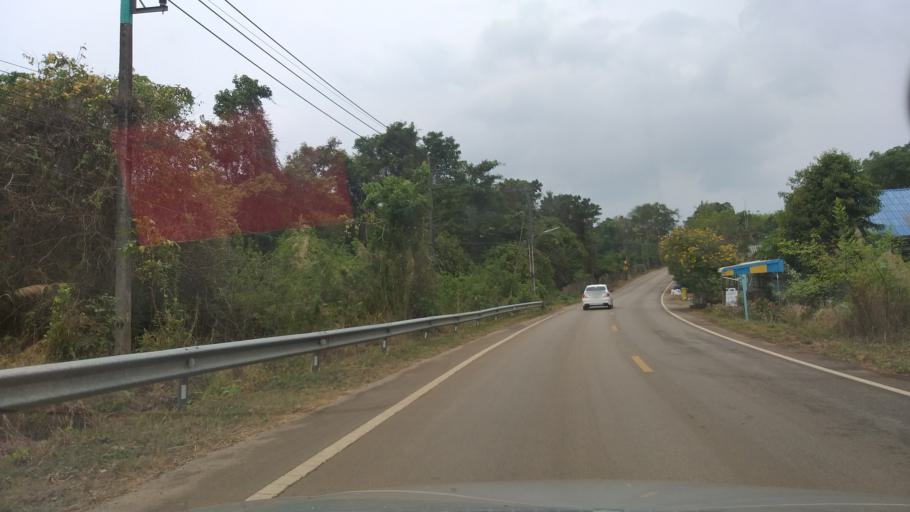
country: TH
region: Trat
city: Laem Ngop
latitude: 12.1923
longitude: 102.2914
